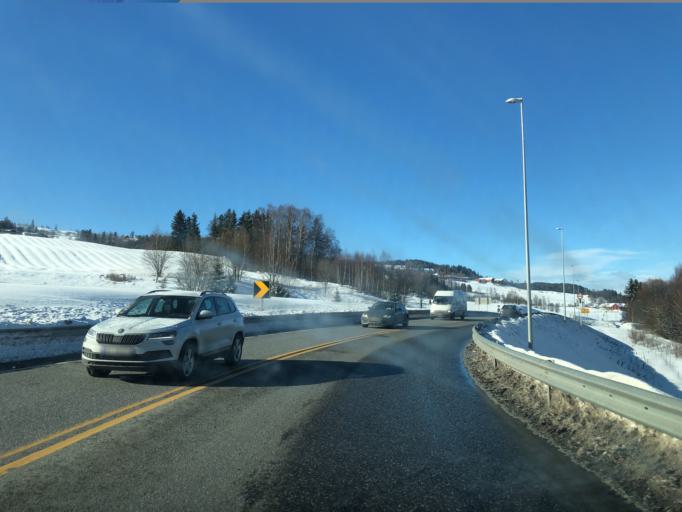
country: NO
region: Oppland
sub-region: Lunner
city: Roa
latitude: 60.3225
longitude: 10.5813
